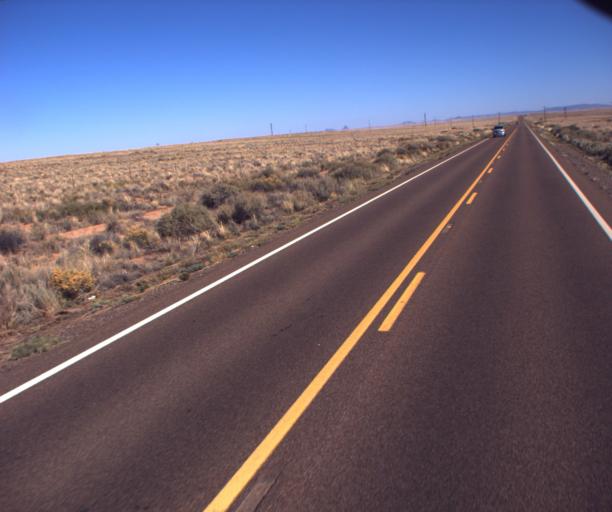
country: US
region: Arizona
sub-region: Navajo County
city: Winslow
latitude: 35.0697
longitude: -110.5731
